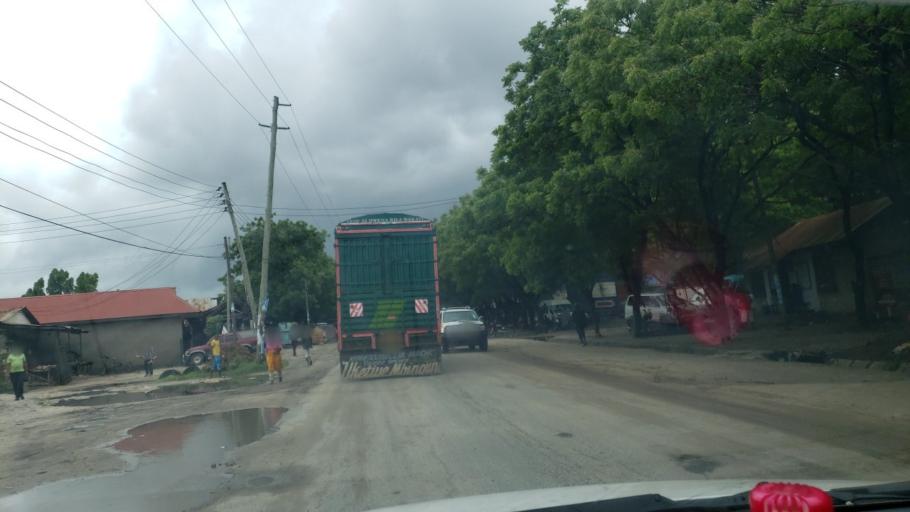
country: TZ
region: Dar es Salaam
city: Magomeni
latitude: -6.8040
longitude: 39.2242
